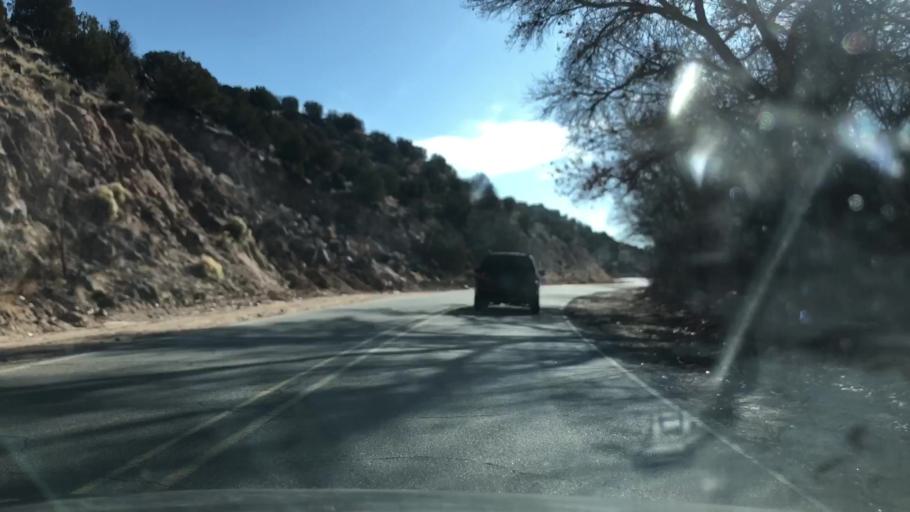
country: US
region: New Mexico
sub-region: Rio Arriba County
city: Ohkay Owingeh
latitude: 36.0882
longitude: -106.1287
